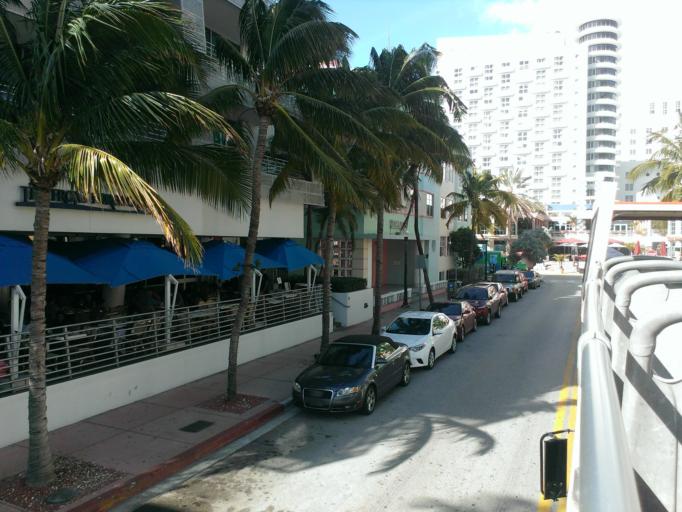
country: US
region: Florida
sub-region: Miami-Dade County
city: Miami Beach
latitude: 25.7870
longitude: -80.1295
